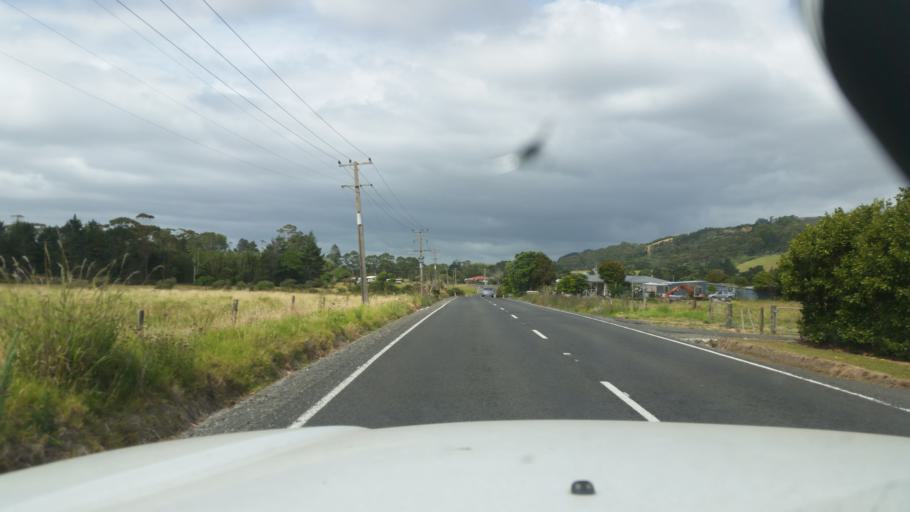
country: NZ
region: Northland
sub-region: Far North District
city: Ahipara
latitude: -35.1769
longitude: 173.1739
